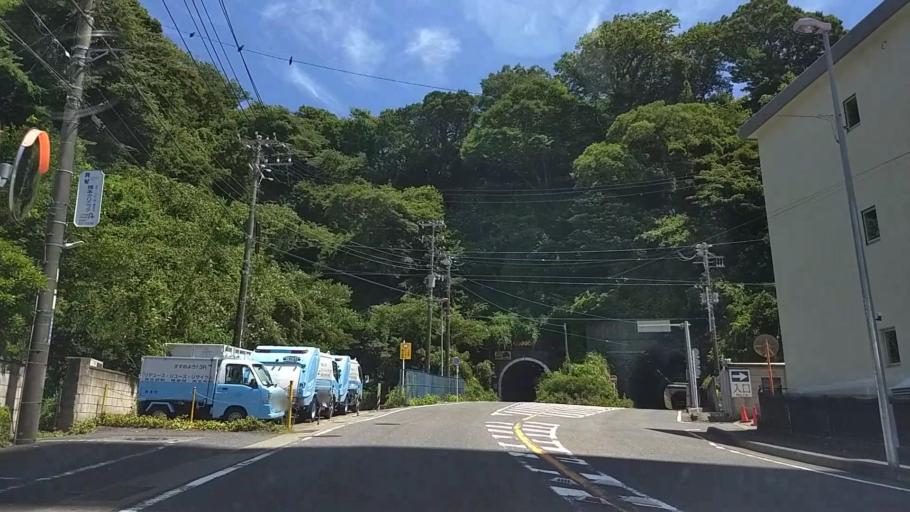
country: JP
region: Kanagawa
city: Kamakura
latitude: 35.3086
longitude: 139.5615
